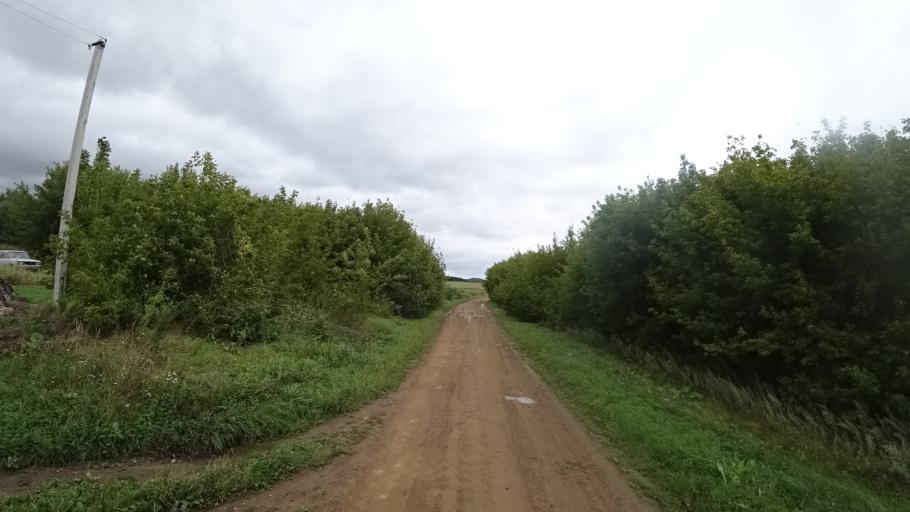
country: RU
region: Primorskiy
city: Chernigovka
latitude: 44.4327
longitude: 132.5922
